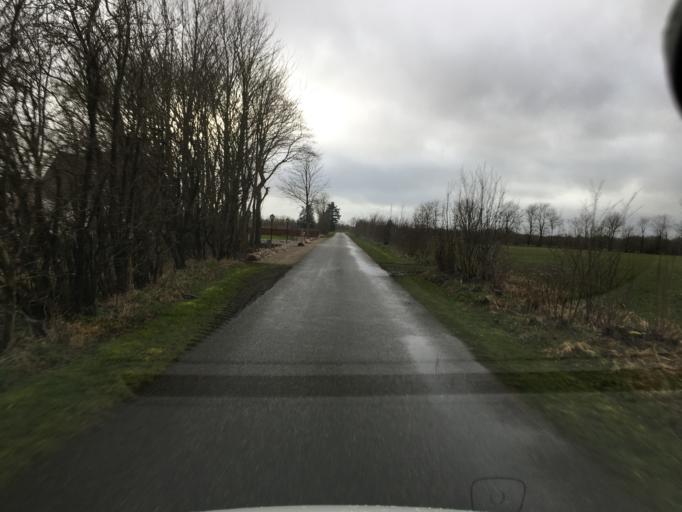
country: DE
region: Schleswig-Holstein
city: Boxlund
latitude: 54.9475
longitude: 9.1325
